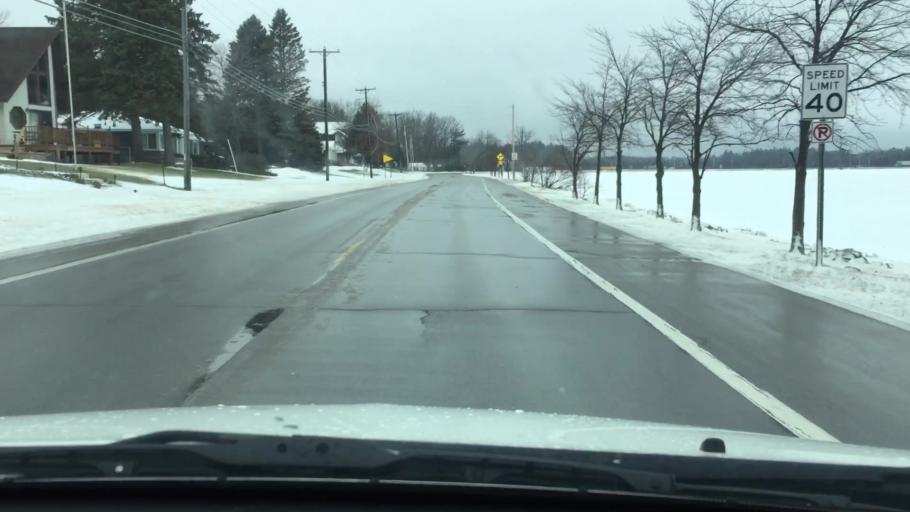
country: US
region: Michigan
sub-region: Wexford County
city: Cadillac
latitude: 44.2322
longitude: -85.4399
